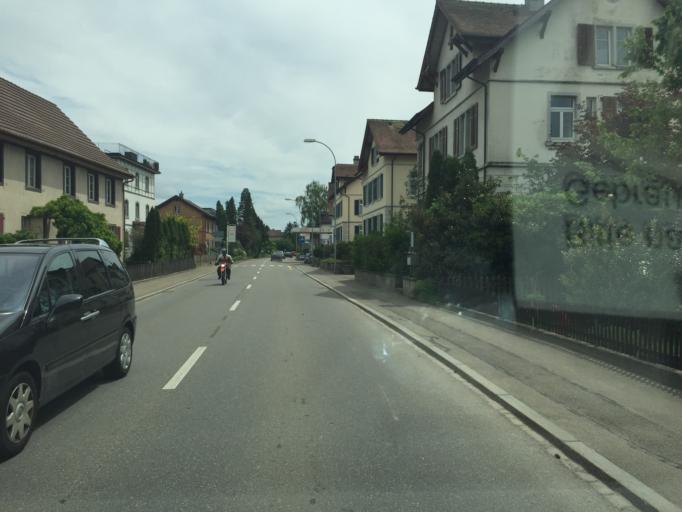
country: CH
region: Thurgau
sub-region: Frauenfeld District
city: Wagenhausen
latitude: 47.6581
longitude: 8.8522
